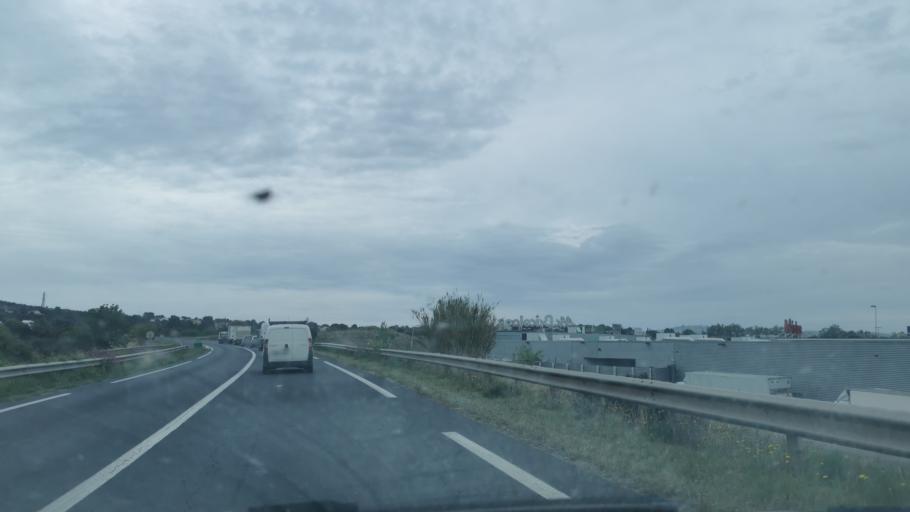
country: FR
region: Languedoc-Roussillon
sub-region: Departement de l'Herault
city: Balaruc-le-Vieux
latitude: 43.4612
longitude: 3.6937
